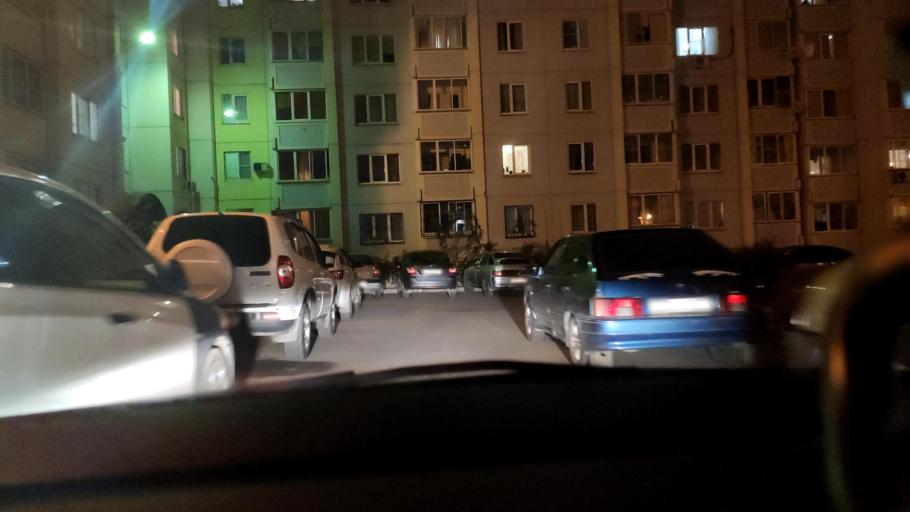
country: RU
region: Voronezj
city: Podgornoye
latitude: 51.7166
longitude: 39.1890
